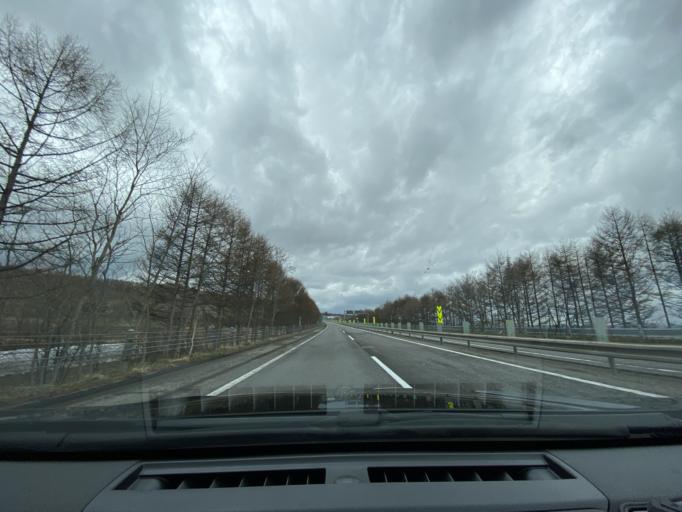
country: JP
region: Hokkaido
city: Fukagawa
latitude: 43.6635
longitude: 142.0175
